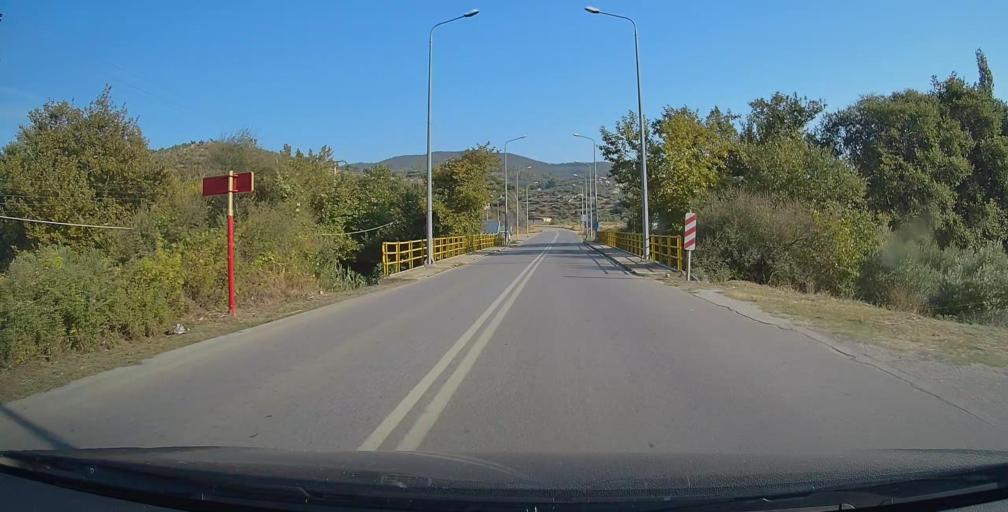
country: GR
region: Central Macedonia
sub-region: Nomos Chalkidikis
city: Neos Marmaras
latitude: 40.0884
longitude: 23.8019
